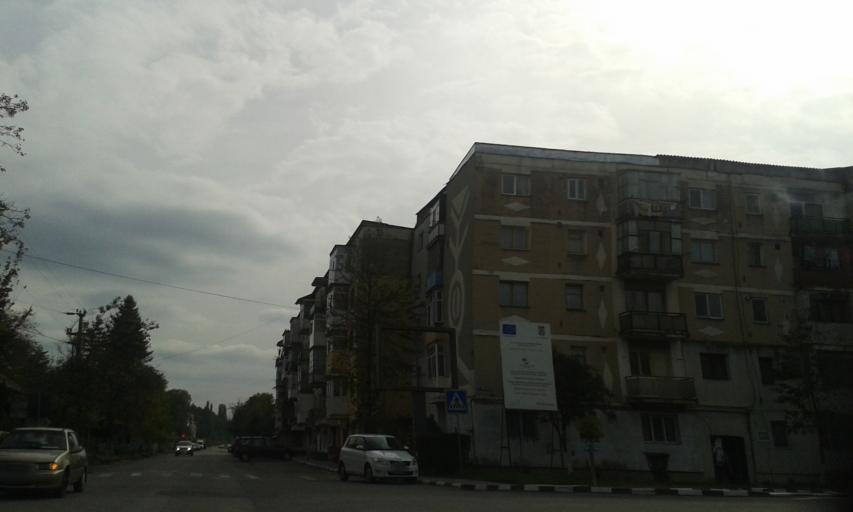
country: RO
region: Gorj
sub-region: Comuna Targu Carbunesti
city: Targu Carbunesti
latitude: 44.9639
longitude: 23.5068
